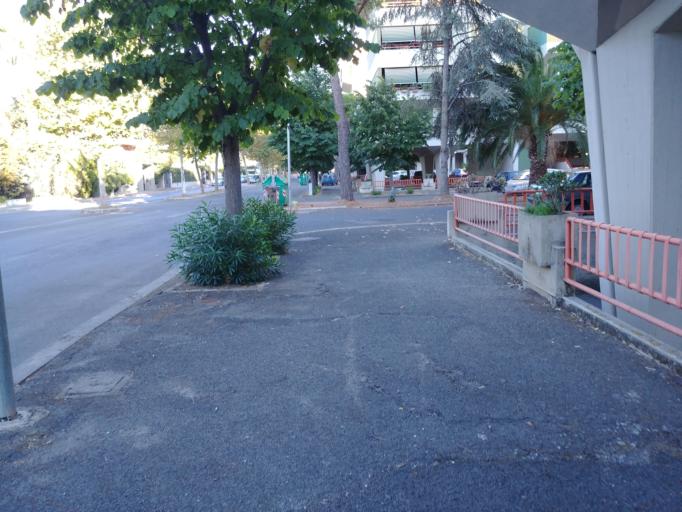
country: IT
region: Latium
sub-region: Provincia di Latina
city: Latina
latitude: 41.4529
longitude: 12.8900
